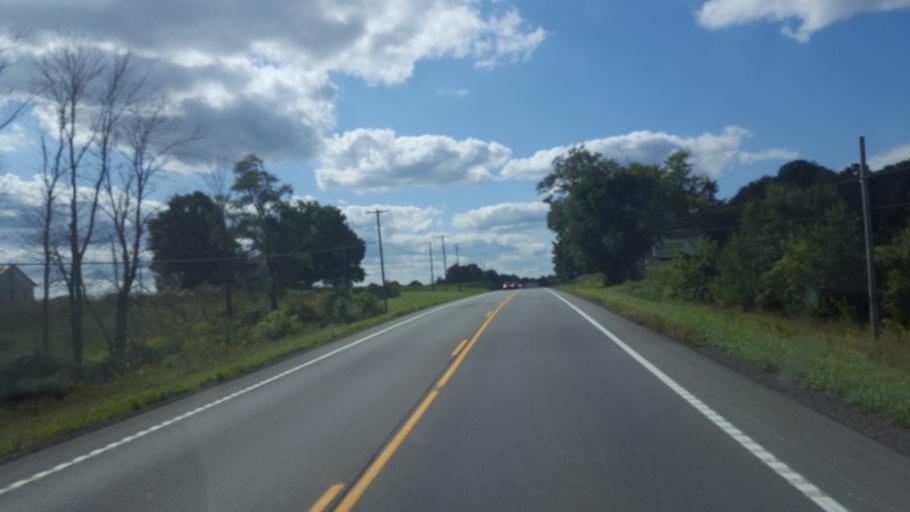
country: US
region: Ohio
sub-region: Ashland County
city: Ashland
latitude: 40.8573
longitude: -82.2386
